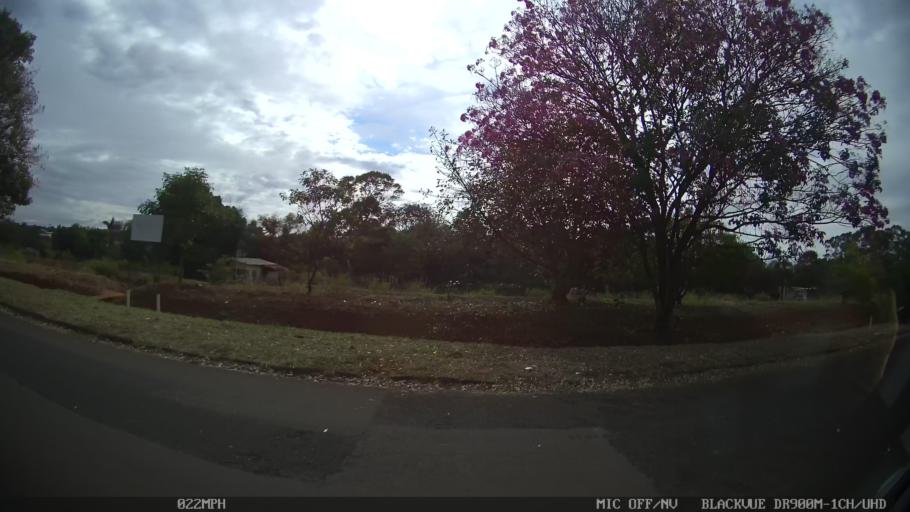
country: BR
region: Sao Paulo
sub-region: Sao Jose Do Rio Preto
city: Sao Jose do Rio Preto
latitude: -20.8136
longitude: -49.3536
